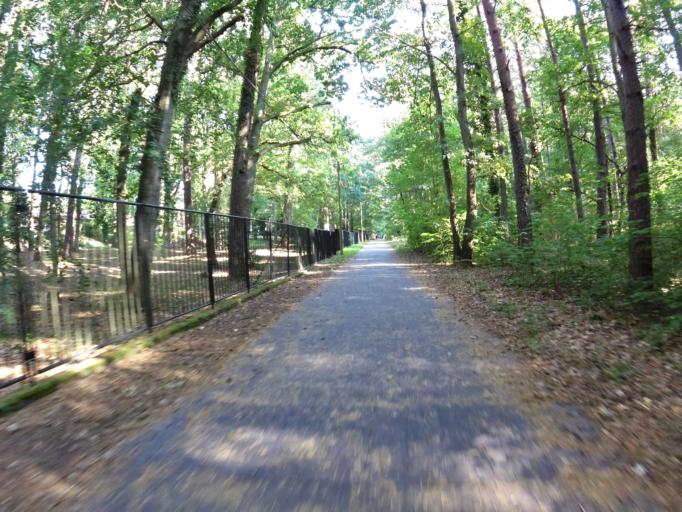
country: DE
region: Mecklenburg-Vorpommern
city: Seebad Heringsdorf
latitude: 53.9339
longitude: 14.2032
